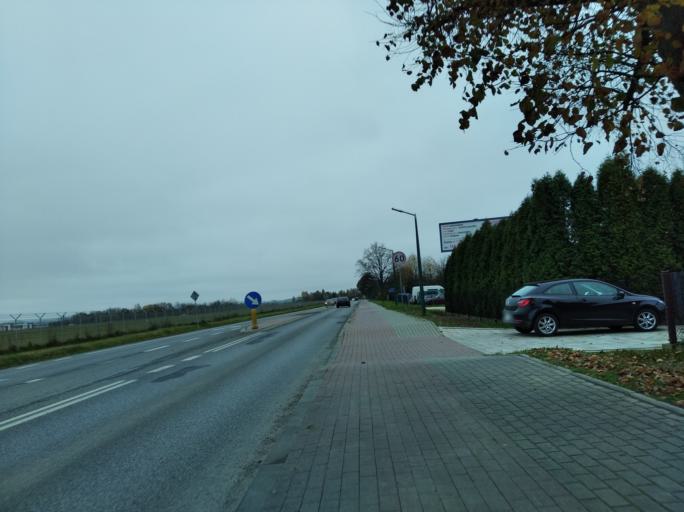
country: PL
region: Subcarpathian Voivodeship
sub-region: Krosno
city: Krosno
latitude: 49.6867
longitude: 21.7244
